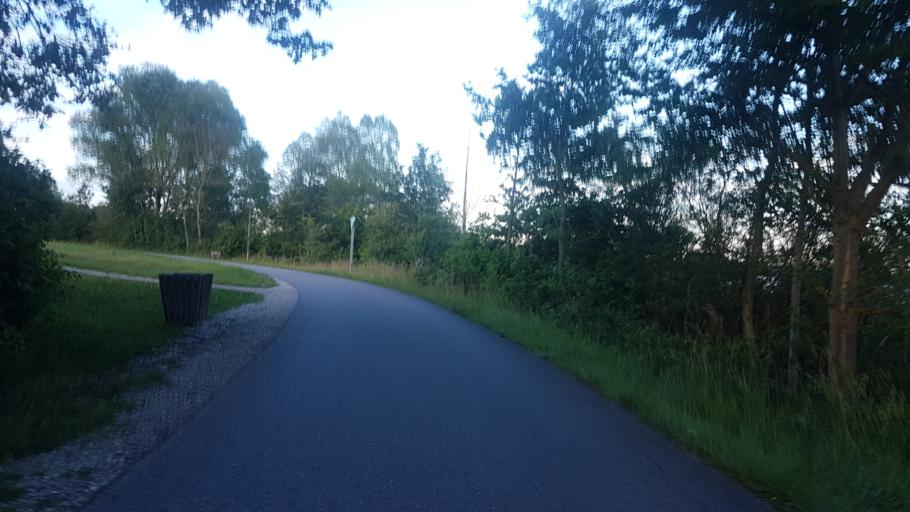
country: DE
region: Bavaria
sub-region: Regierungsbezirk Mittelfranken
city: Muhr am See
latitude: 49.1410
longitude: 10.6975
